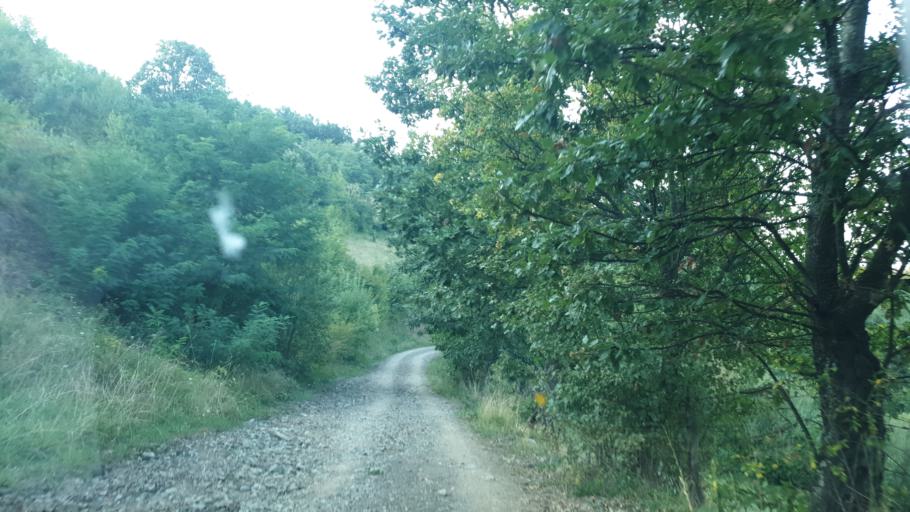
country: RS
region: Central Serbia
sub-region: Zlatiborski Okrug
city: Kosjeric
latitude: 44.0087
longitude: 19.9923
